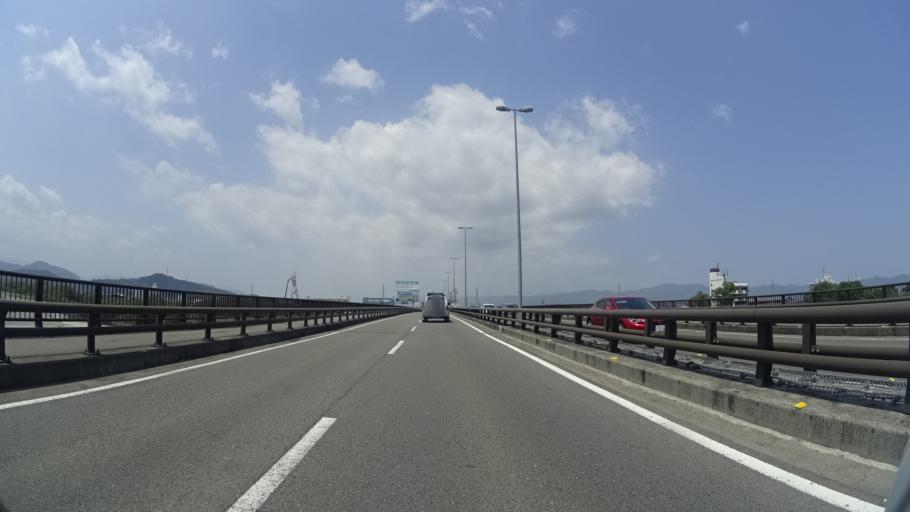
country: JP
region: Tokushima
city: Ishii
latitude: 34.0727
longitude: 134.4988
